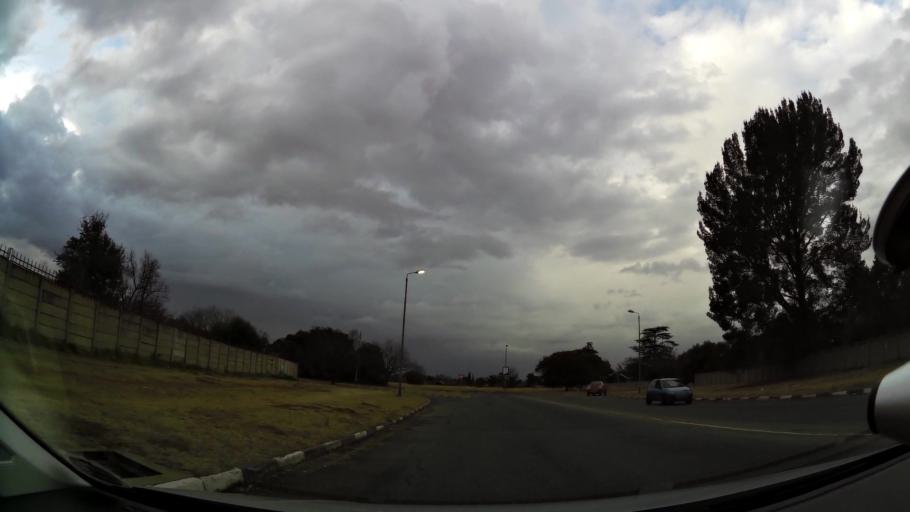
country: ZA
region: Orange Free State
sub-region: Lejweleputswa District Municipality
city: Welkom
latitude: -27.9573
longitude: 26.7283
